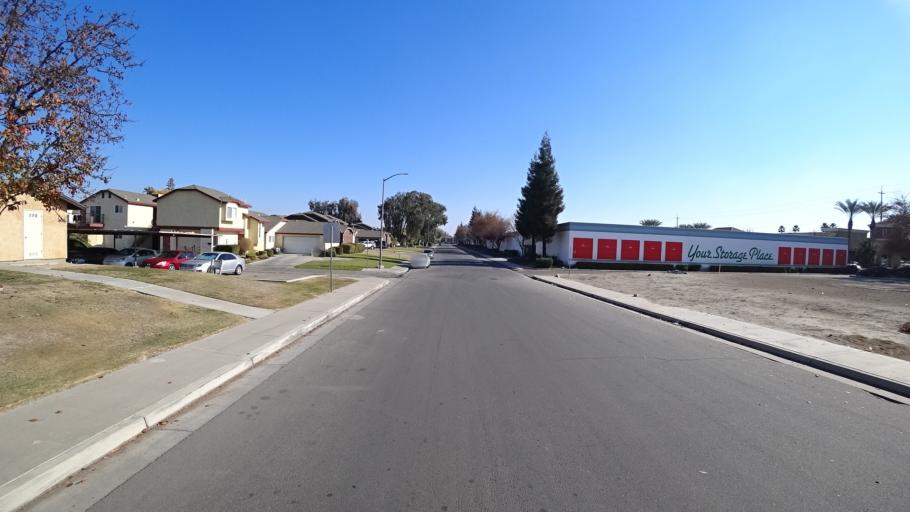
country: US
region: California
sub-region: Kern County
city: Greenfield
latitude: 35.2972
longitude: -119.0563
